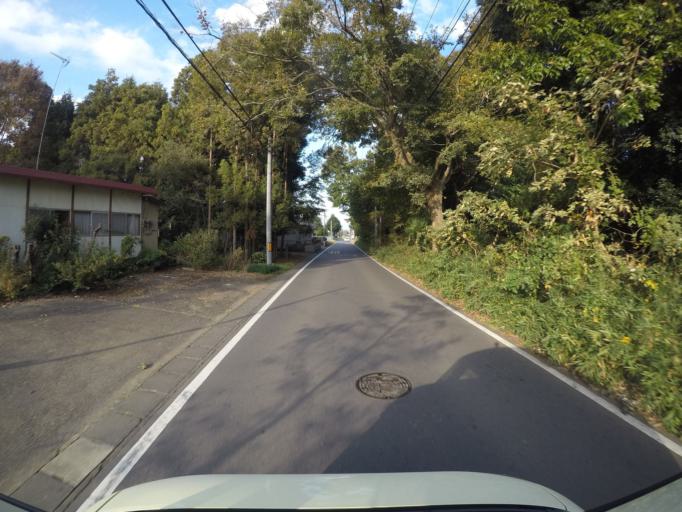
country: JP
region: Ibaraki
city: Naka
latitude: 36.0512
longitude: 140.0834
